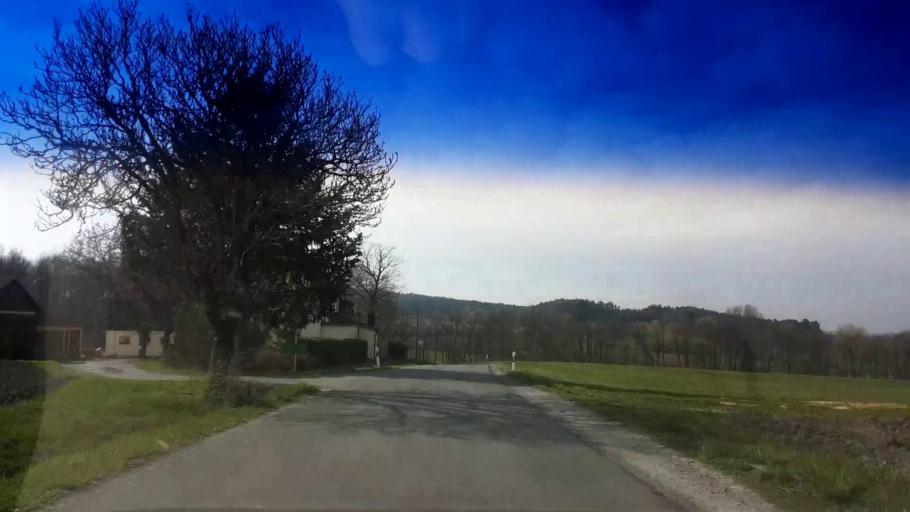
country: DE
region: Bavaria
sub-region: Upper Franconia
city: Gesees
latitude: 50.0296
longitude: 11.6278
